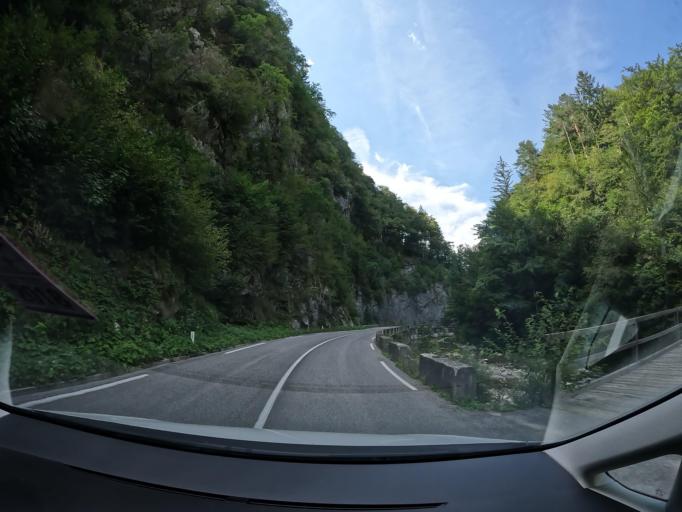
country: SI
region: Jezersko
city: Zgornje Jezersko
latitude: 46.3419
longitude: 14.4846
